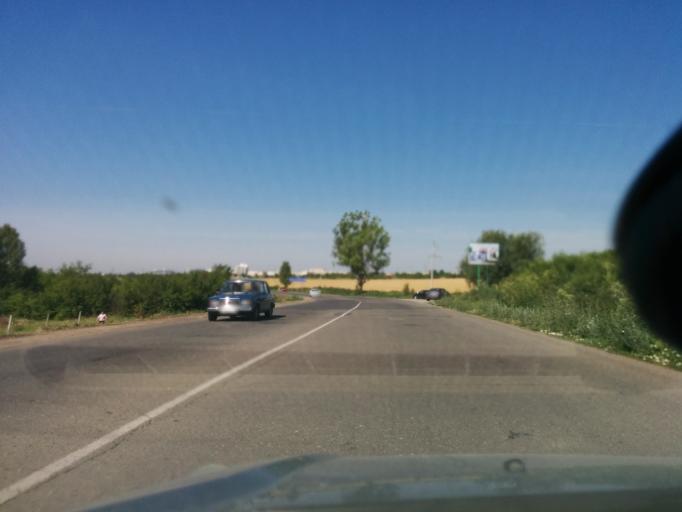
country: MD
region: Chisinau
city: Stauceni
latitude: 47.0483
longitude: 28.9166
